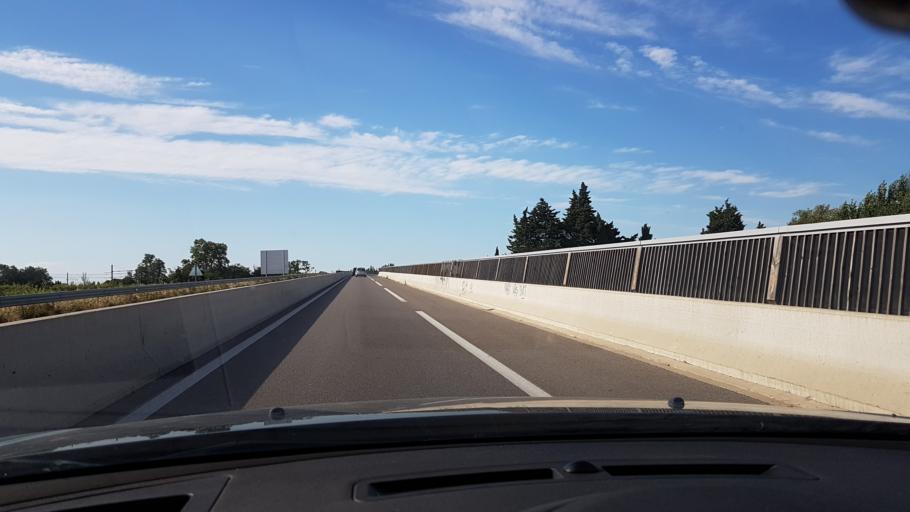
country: FR
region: Provence-Alpes-Cote d'Azur
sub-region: Departement des Bouches-du-Rhone
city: Rognonas
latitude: 43.8972
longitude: 4.7858
